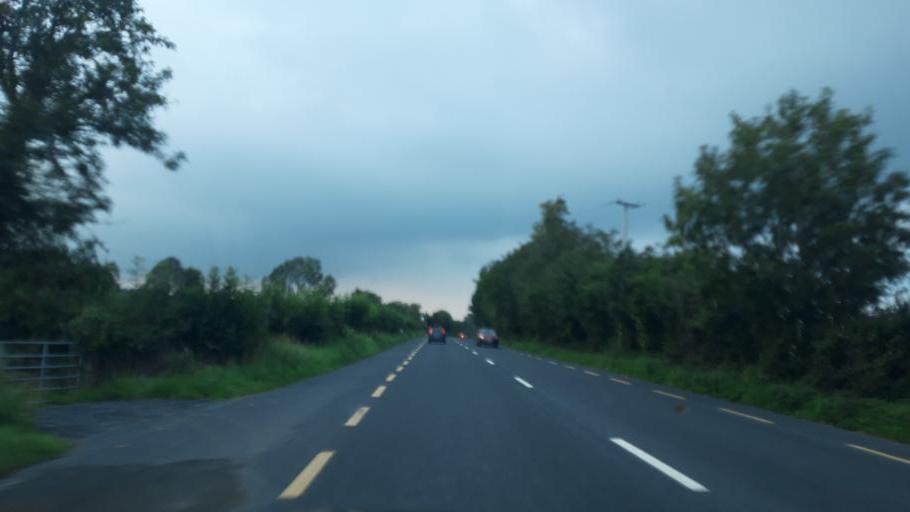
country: IE
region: Leinster
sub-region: Kilkenny
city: Thomastown
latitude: 52.5483
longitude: -7.1294
